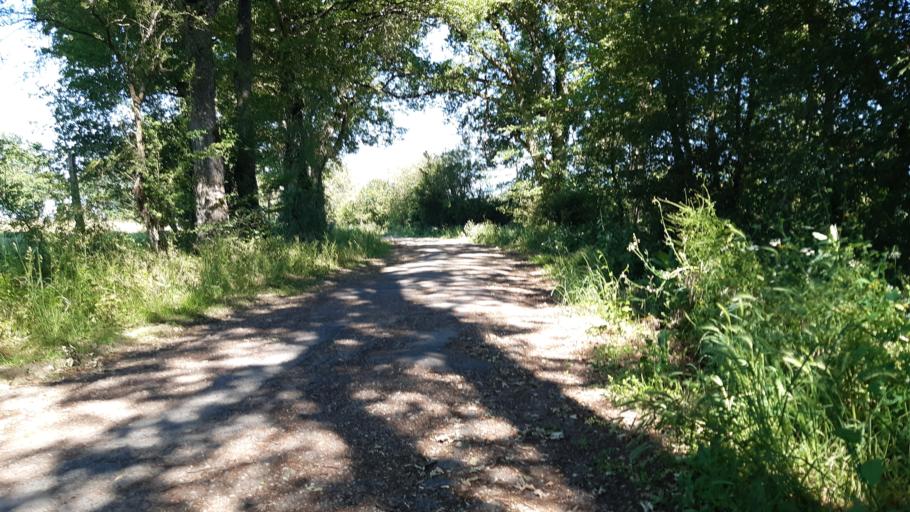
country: FR
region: Centre
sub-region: Departement d'Indre-et-Loire
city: Mettray
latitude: 47.4345
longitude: 0.6580
